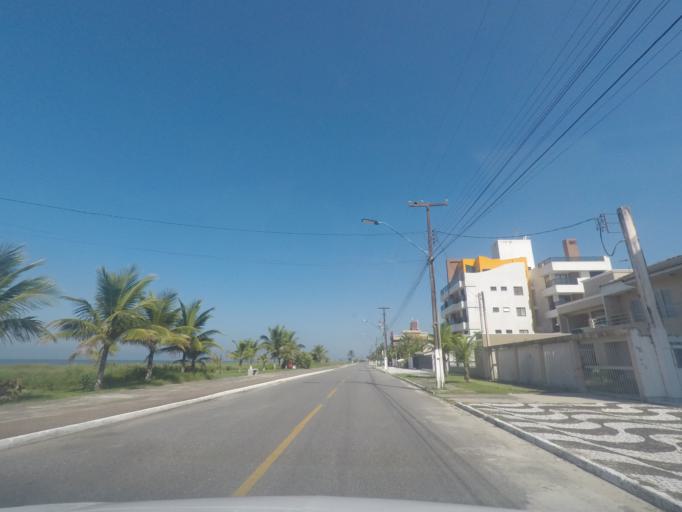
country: BR
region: Parana
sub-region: Pontal Do Parana
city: Pontal do Parana
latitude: -25.7254
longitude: -48.4854
